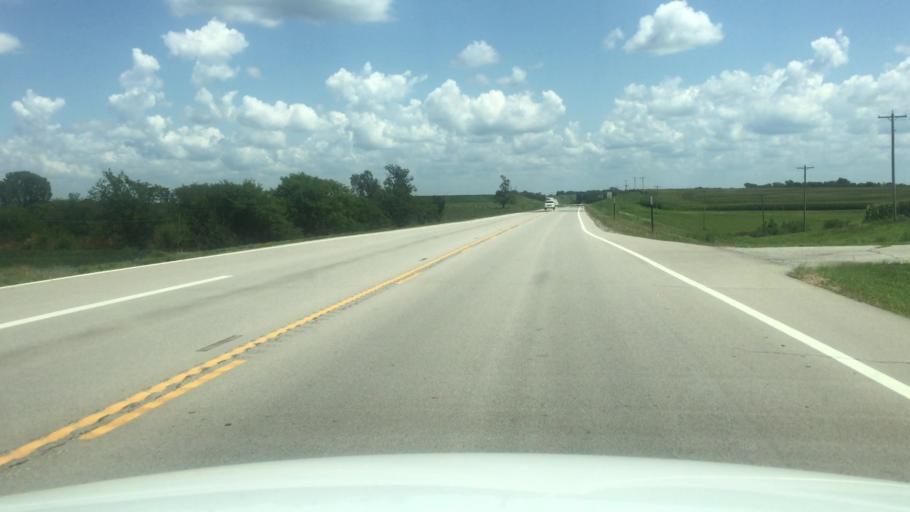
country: US
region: Kansas
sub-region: Brown County
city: Horton
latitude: 39.6675
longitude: -95.4883
